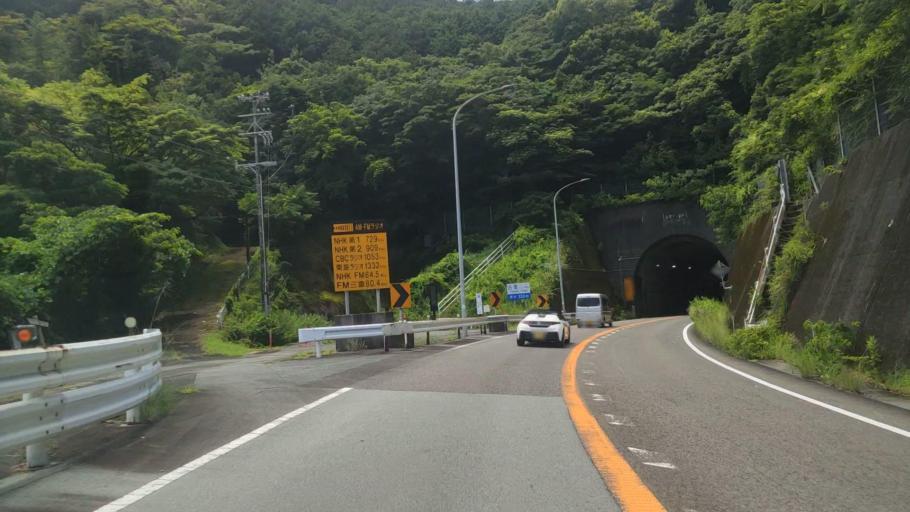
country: JP
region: Mie
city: Owase
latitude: 34.1792
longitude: 136.3012
